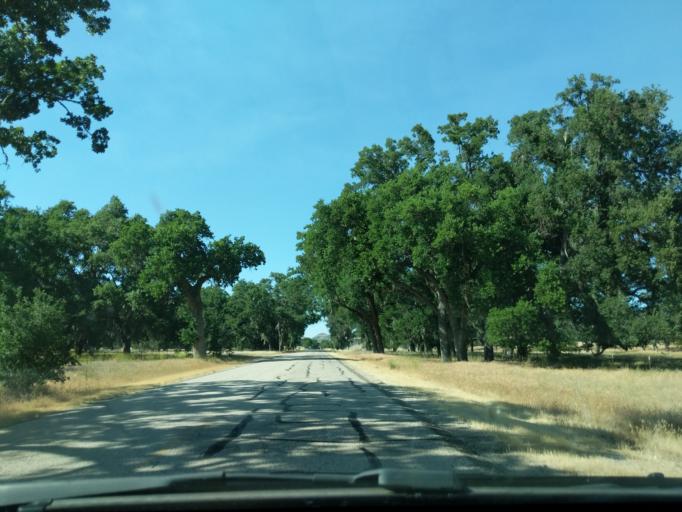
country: US
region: California
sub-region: Monterey County
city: King City
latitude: 36.0181
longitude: -121.1785
